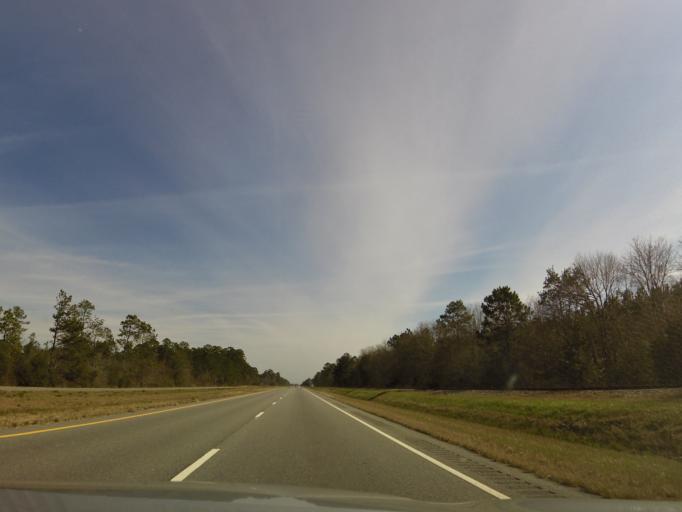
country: US
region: Georgia
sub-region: Lowndes County
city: Valdosta
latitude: 30.8885
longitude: -83.1289
